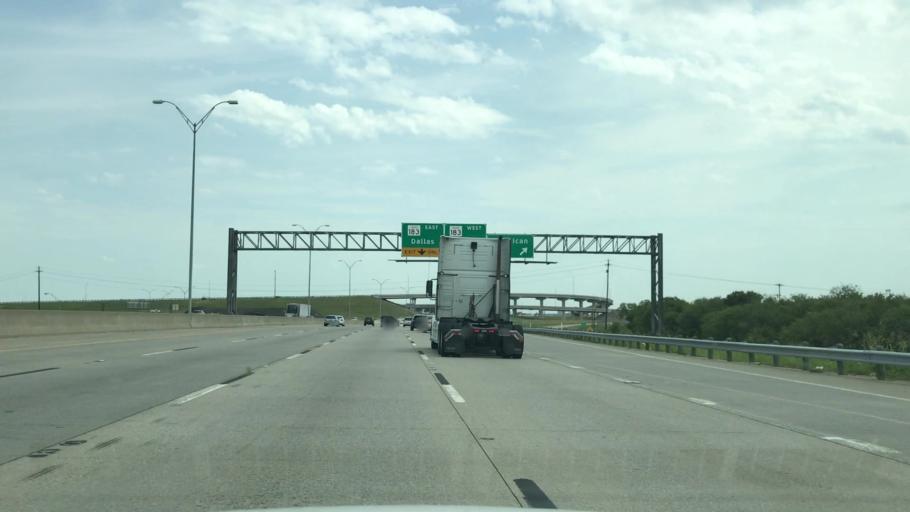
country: US
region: Texas
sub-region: Tarrant County
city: Euless
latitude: 32.8447
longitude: -97.0622
